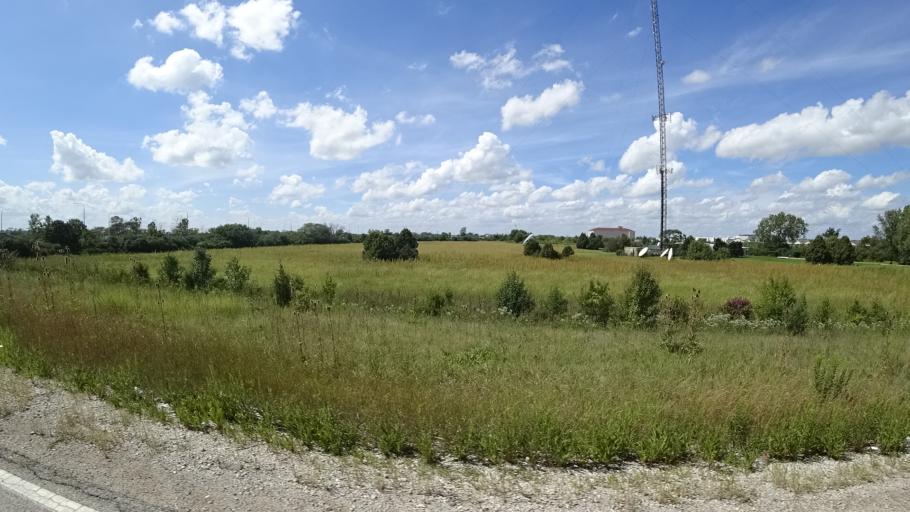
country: US
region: Illinois
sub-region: Cook County
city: Tinley Park
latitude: 41.5526
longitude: -87.7836
